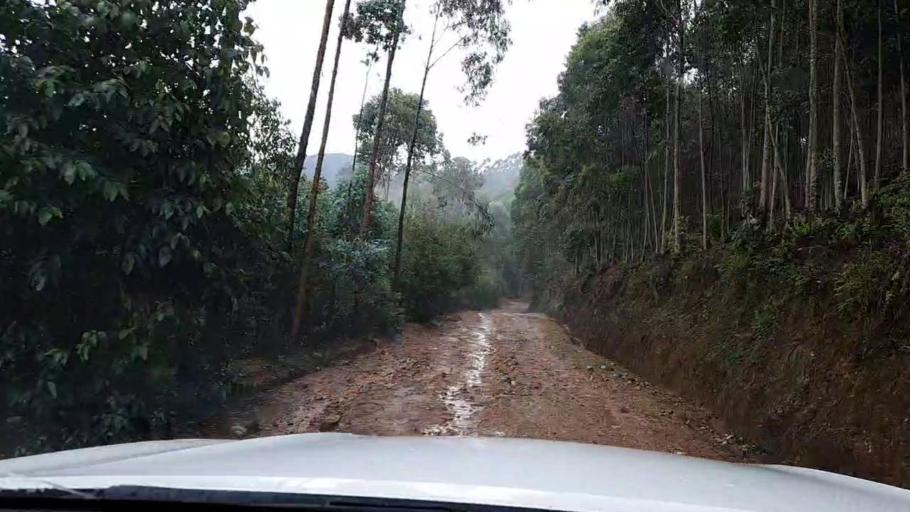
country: RW
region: Western Province
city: Cyangugu
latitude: -2.5505
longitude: 28.9778
